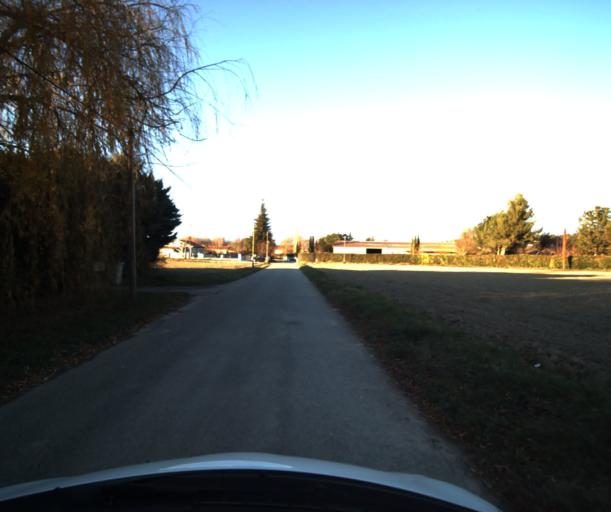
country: FR
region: Provence-Alpes-Cote d'Azur
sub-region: Departement du Vaucluse
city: Pertuis
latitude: 43.6775
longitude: 5.5118
